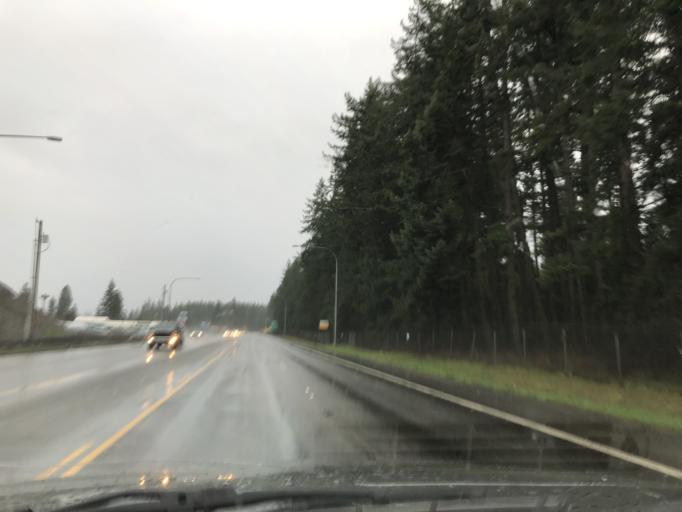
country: US
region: Washington
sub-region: Pierce County
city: Spanaway
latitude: 47.0891
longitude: -122.4350
